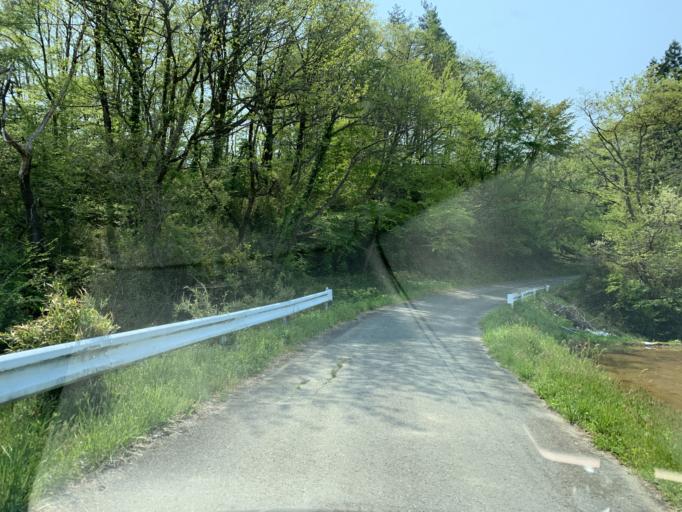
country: JP
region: Iwate
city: Ichinoseki
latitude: 38.8899
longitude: 141.0583
